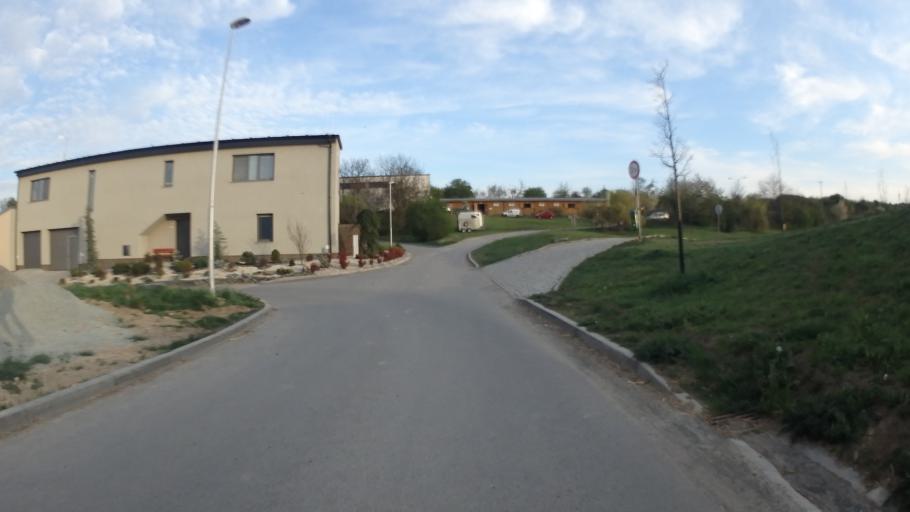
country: CZ
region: South Moravian
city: Moravany
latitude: 49.1440
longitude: 16.5739
